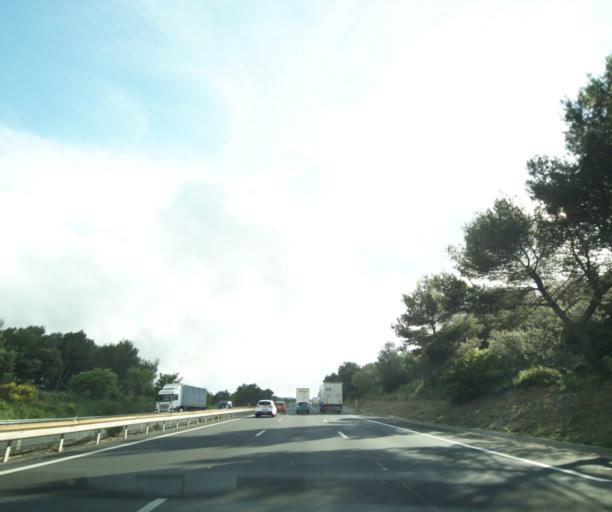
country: FR
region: Languedoc-Roussillon
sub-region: Departement de l'Herault
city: Fabregues
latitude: 43.5275
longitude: 3.7687
